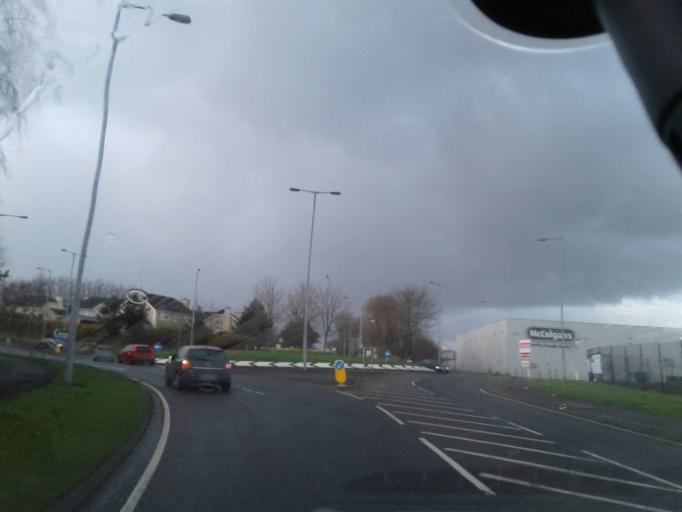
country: GB
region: Northern Ireland
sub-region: Strabane District
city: Strabane
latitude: 54.8064
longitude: -7.4730
